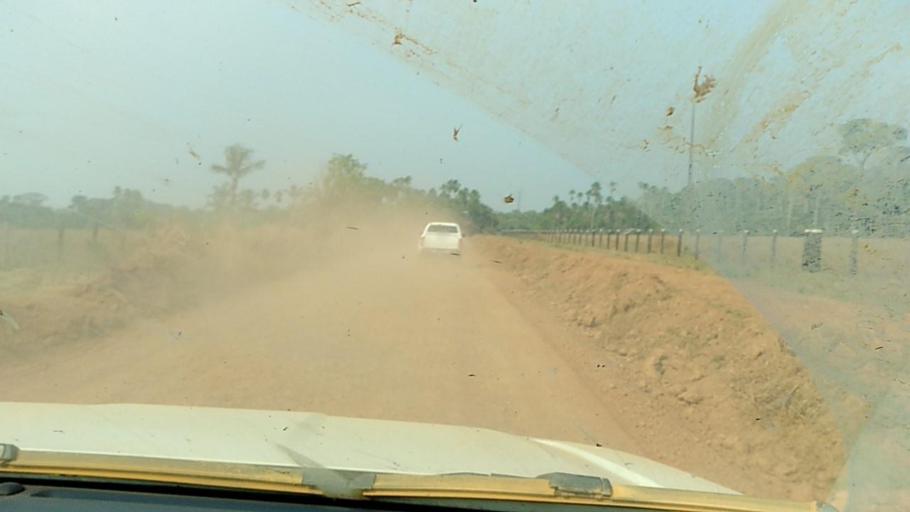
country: BR
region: Rondonia
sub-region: Porto Velho
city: Porto Velho
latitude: -8.7859
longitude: -64.0916
